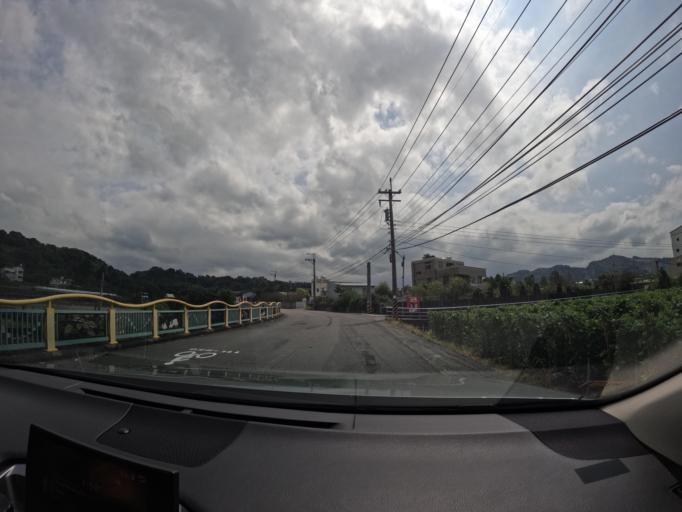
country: TW
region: Taiwan
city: Fengyuan
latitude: 24.3075
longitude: 120.8360
